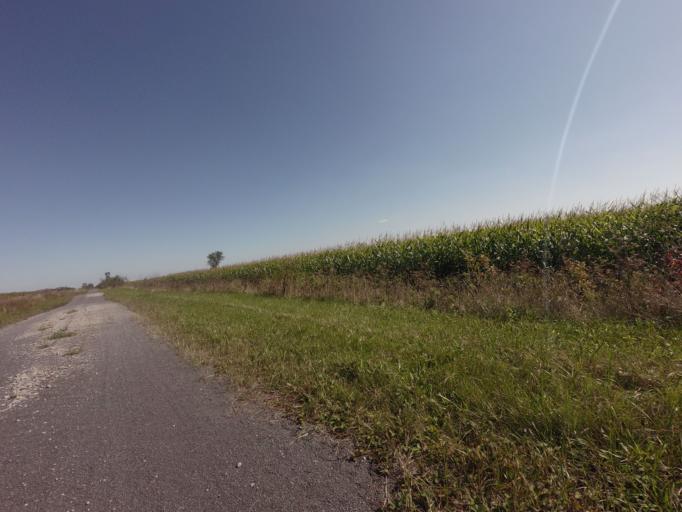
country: CA
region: Quebec
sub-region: Outaouais
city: Papineauville
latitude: 45.5419
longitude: -74.8350
